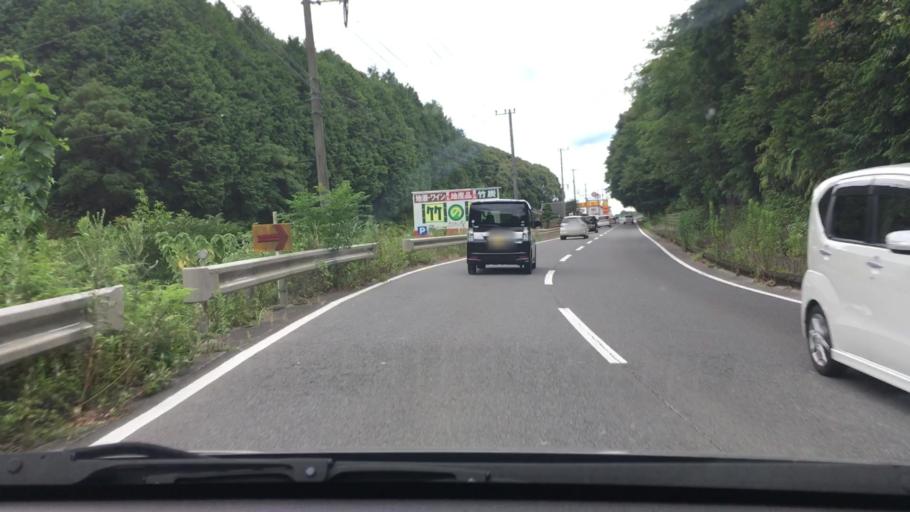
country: JP
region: Nagasaki
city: Togitsu
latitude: 32.9731
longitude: 129.7818
